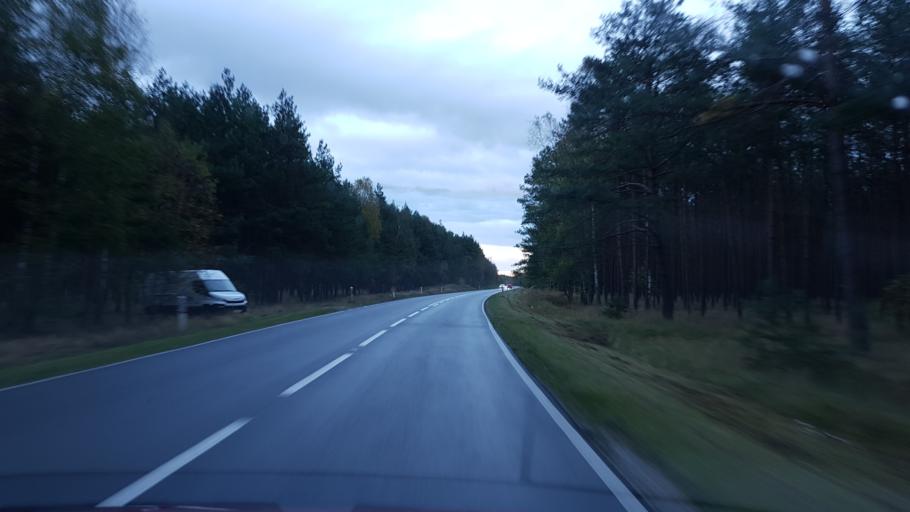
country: PL
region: Greater Poland Voivodeship
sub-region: Powiat pilski
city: Pila
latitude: 53.1978
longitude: 16.8294
